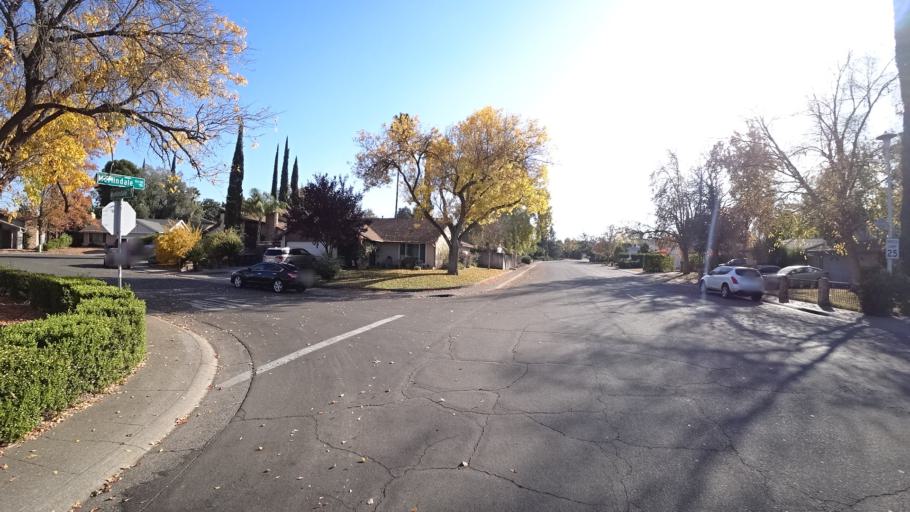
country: US
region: California
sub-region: Sacramento County
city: Citrus Heights
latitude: 38.6770
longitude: -121.2780
